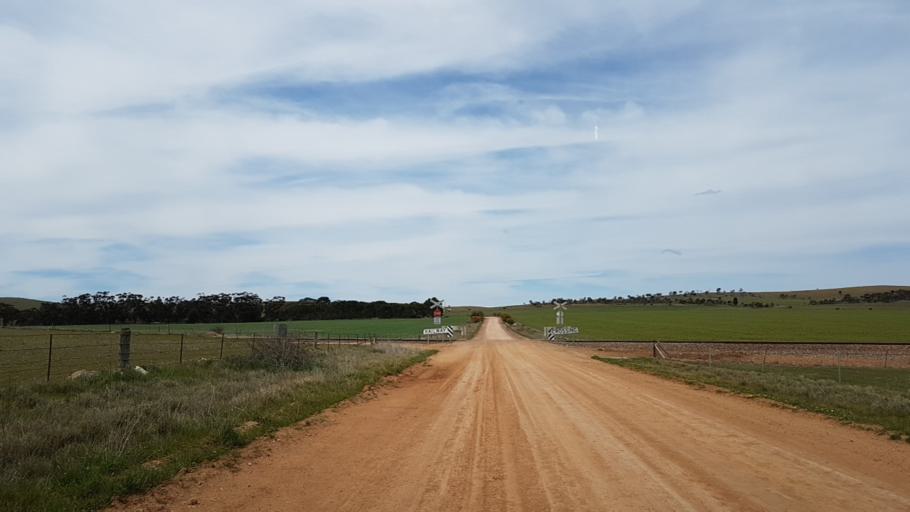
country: AU
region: South Australia
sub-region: Northern Areas
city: Jamestown
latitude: -33.1076
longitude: 138.6227
